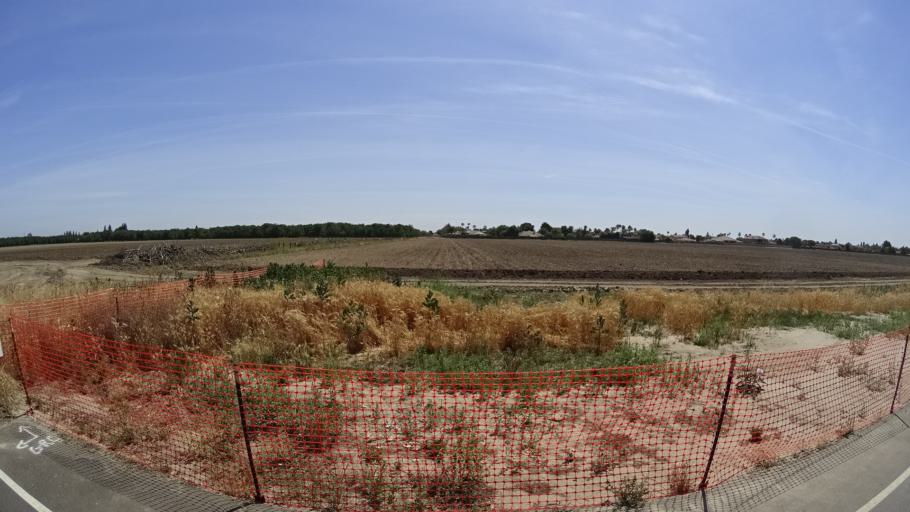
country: US
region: California
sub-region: Kings County
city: Lucerne
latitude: 36.3535
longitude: -119.6819
